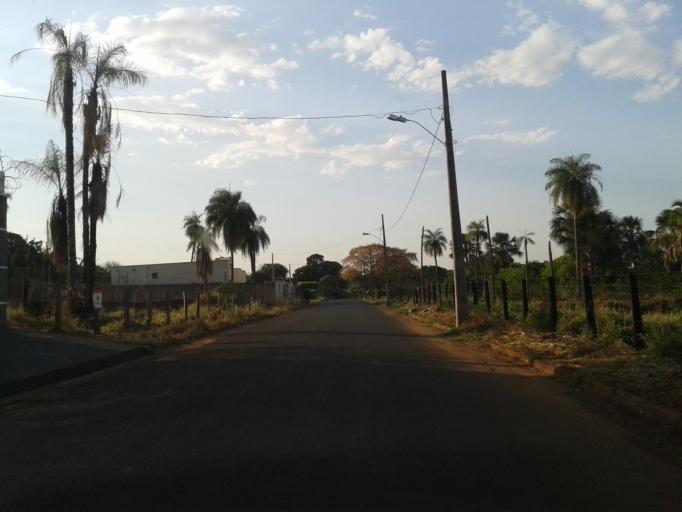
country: BR
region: Minas Gerais
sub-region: Ituiutaba
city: Ituiutaba
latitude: -18.9836
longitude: -49.4452
